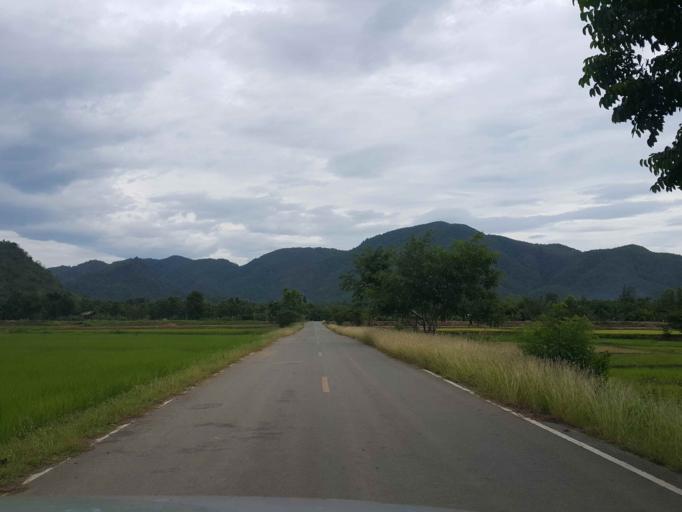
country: TH
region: Sukhothai
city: Thung Saliam
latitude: 17.3374
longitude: 99.4395
